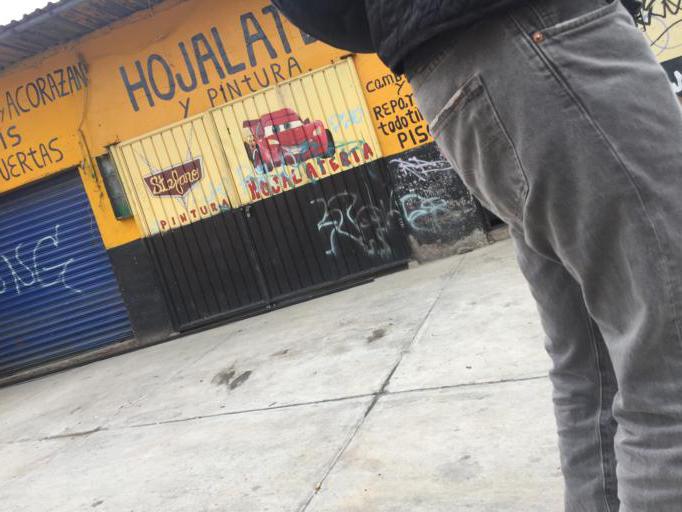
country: MX
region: Mexico
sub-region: Tlalnepantla de Baz
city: Puerto Escondido (Tepeolulco Puerto Escondido)
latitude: 19.5535
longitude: -99.0779
